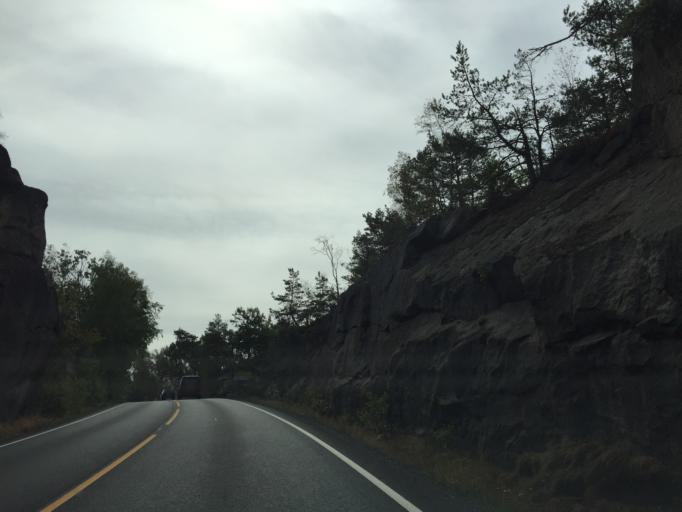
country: NO
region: Ostfold
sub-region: Fredrikstad
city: Fredrikstad
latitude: 59.0994
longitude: 10.9070
